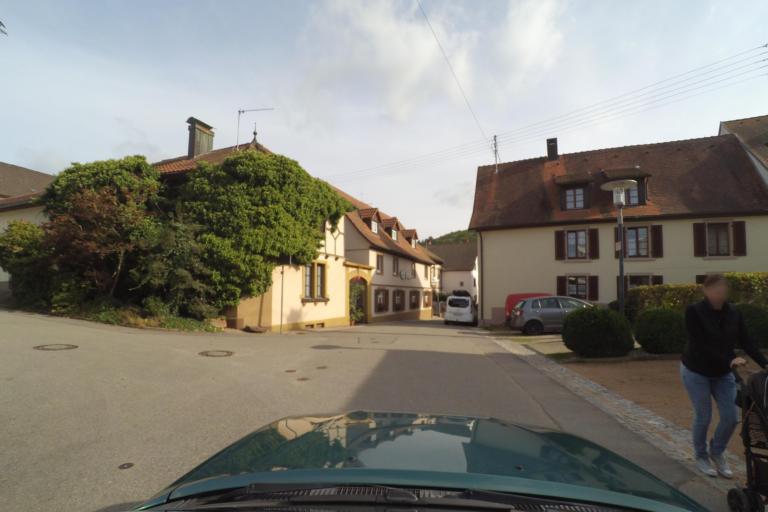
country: DE
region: Baden-Wuerttemberg
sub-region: Freiburg Region
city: Kandern
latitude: 47.7153
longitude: 7.6618
